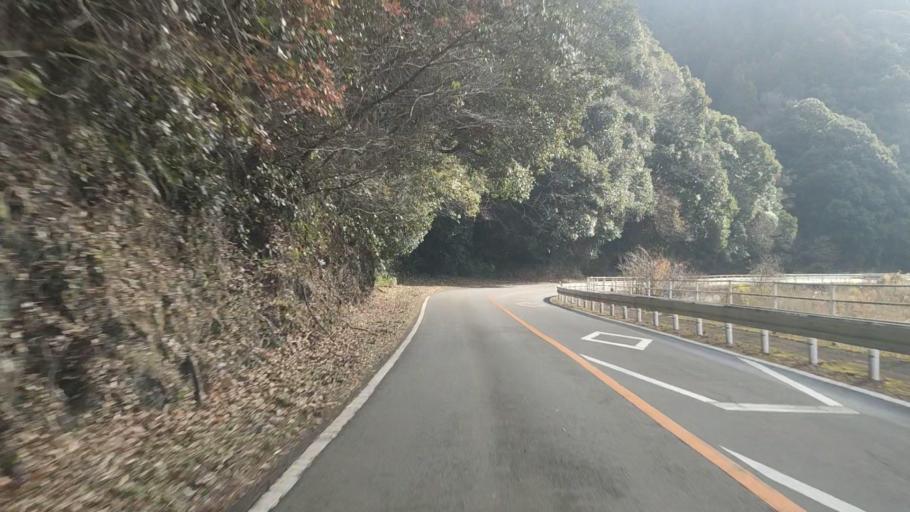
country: JP
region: Kumamoto
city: Hitoyoshi
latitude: 32.3020
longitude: 130.8452
